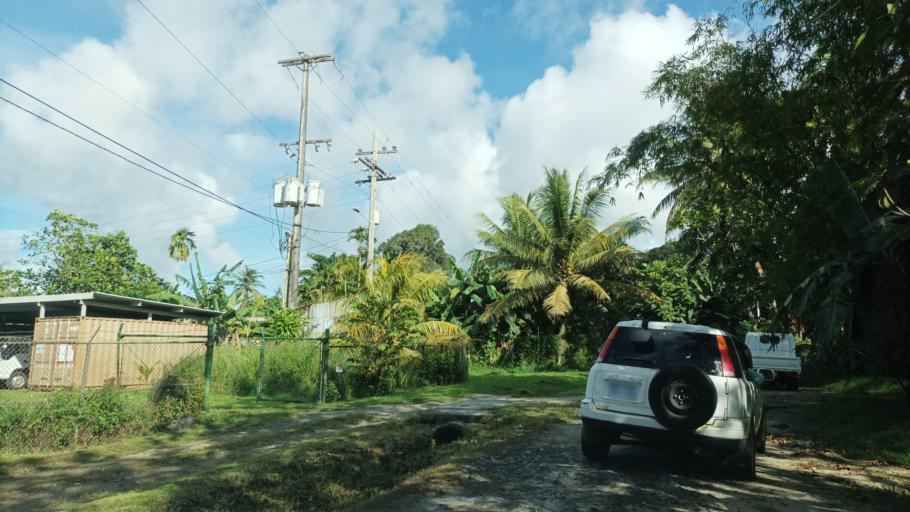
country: FM
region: Pohnpei
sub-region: Kolonia Municipality
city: Kolonia Town
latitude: 6.9683
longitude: 158.2054
